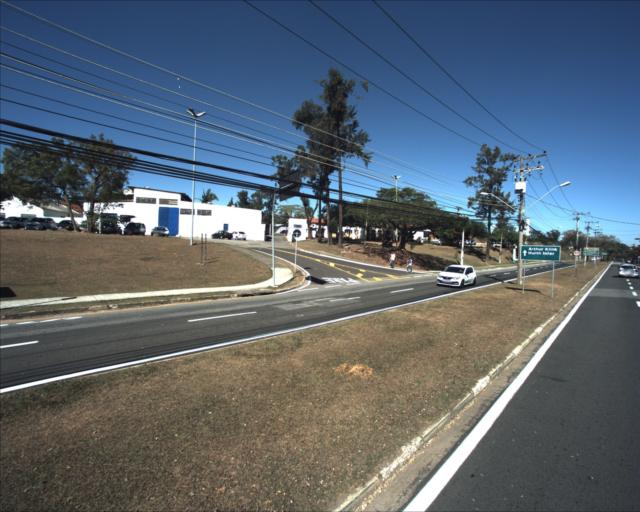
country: BR
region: Sao Paulo
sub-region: Sorocaba
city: Sorocaba
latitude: -23.4737
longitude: -47.4235
